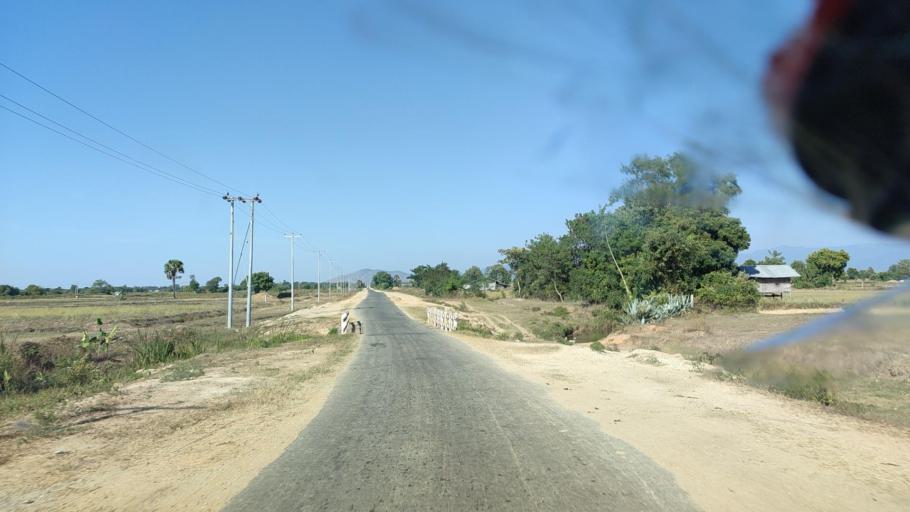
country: MM
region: Mandalay
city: Yamethin
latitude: 20.1730
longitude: 96.2617
